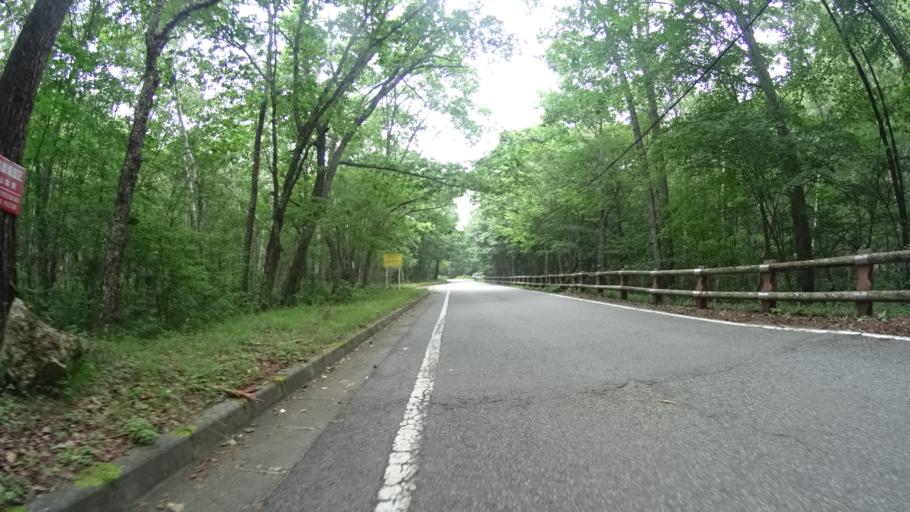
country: JP
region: Yamanashi
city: Nirasaki
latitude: 35.8901
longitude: 138.5677
